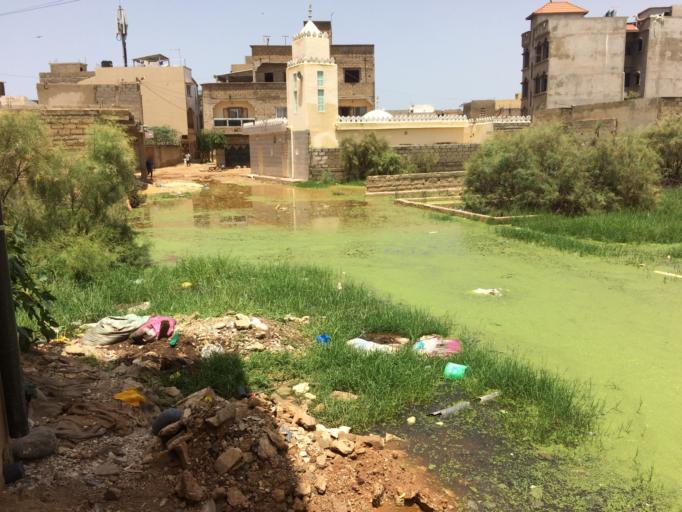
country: SN
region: Dakar
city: Pikine
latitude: 14.7372
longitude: -17.3326
